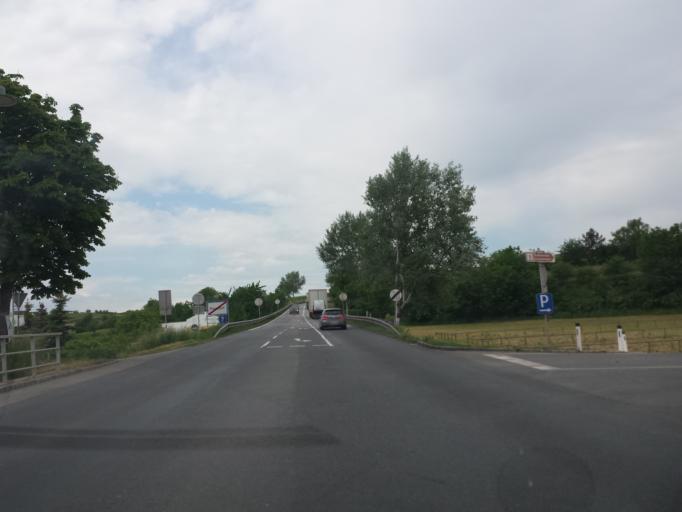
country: AT
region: Lower Austria
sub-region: Politischer Bezirk Mistelbach
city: Poysdorf
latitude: 48.6740
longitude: 16.6286
